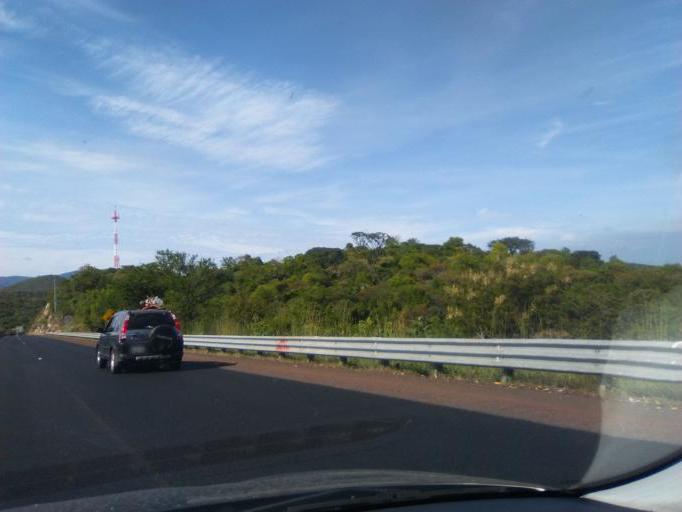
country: MX
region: Guerrero
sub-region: Huitzuco de los Figueroa
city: Ciudad de Huitzuco
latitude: 18.2152
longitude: -99.2154
